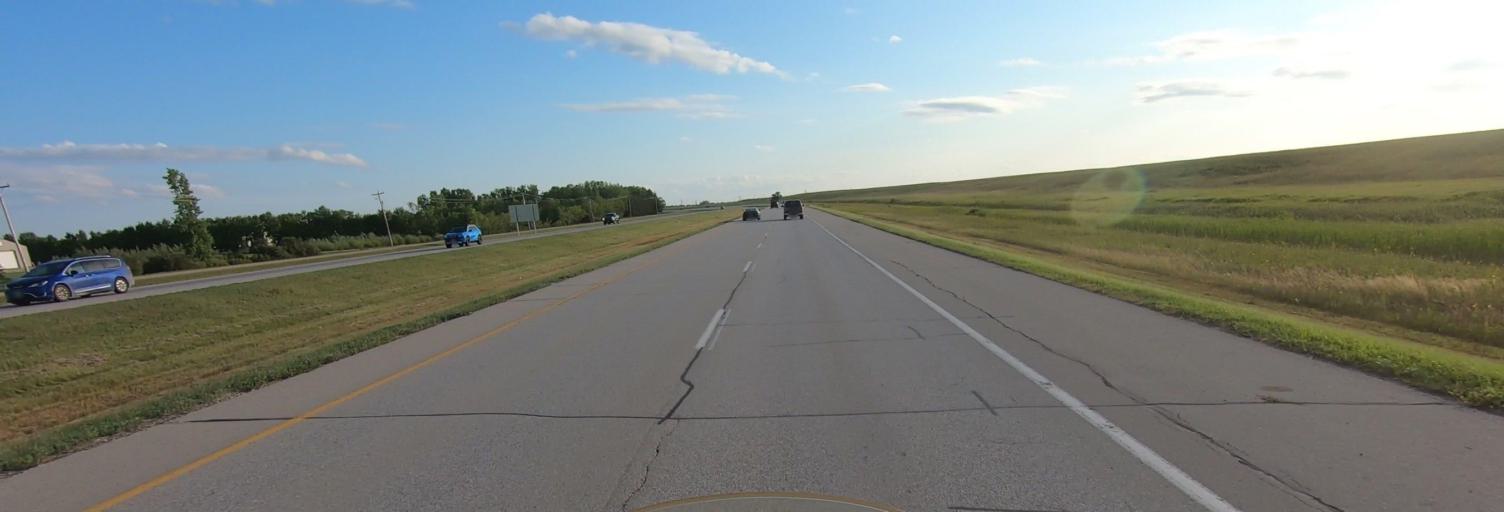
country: CA
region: Manitoba
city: Selkirk
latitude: 49.9967
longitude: -96.9714
